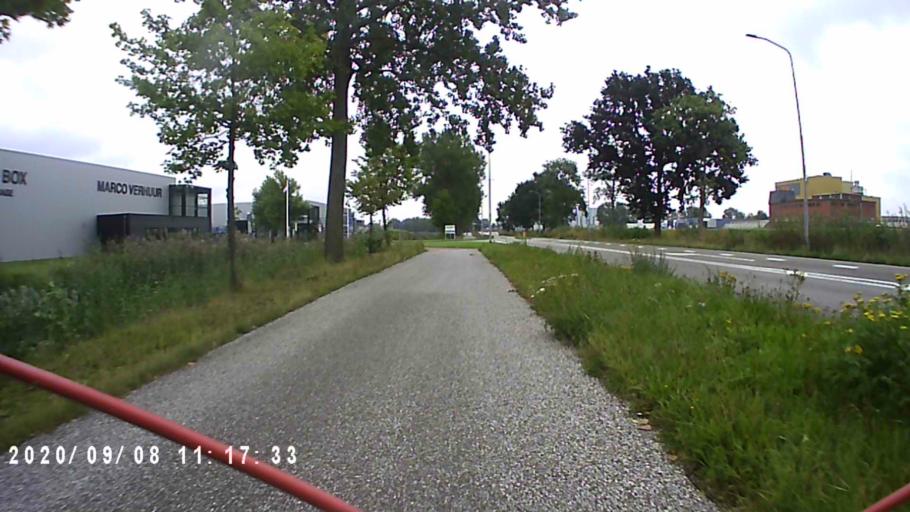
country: NL
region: Groningen
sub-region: Gemeente Hoogezand-Sappemeer
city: Hoogezand
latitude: 53.1701
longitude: 6.7375
